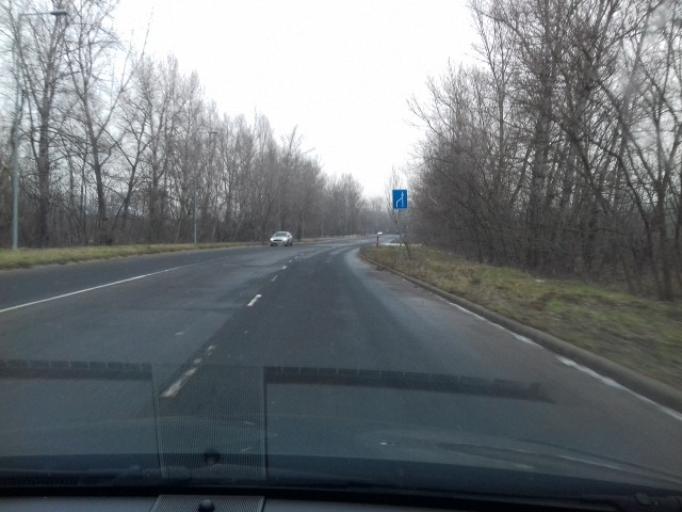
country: HU
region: Budapest
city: Budapest XV. keruelet
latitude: 47.5972
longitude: 19.1079
